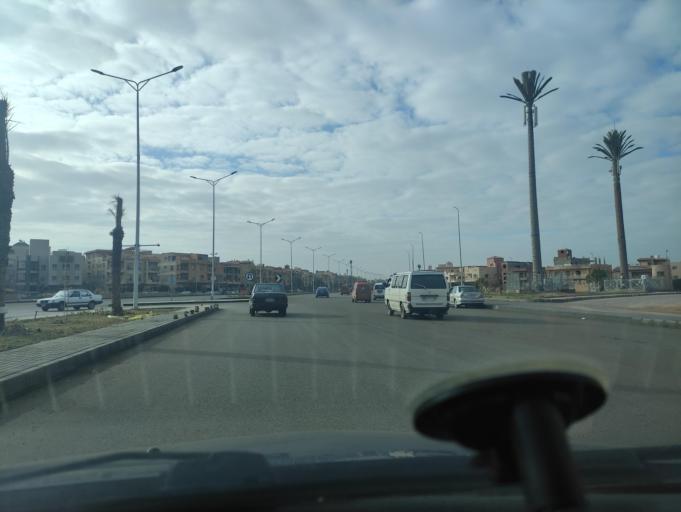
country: EG
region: Muhafazat al Qalyubiyah
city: Al Khankah
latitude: 30.0476
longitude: 31.4424
